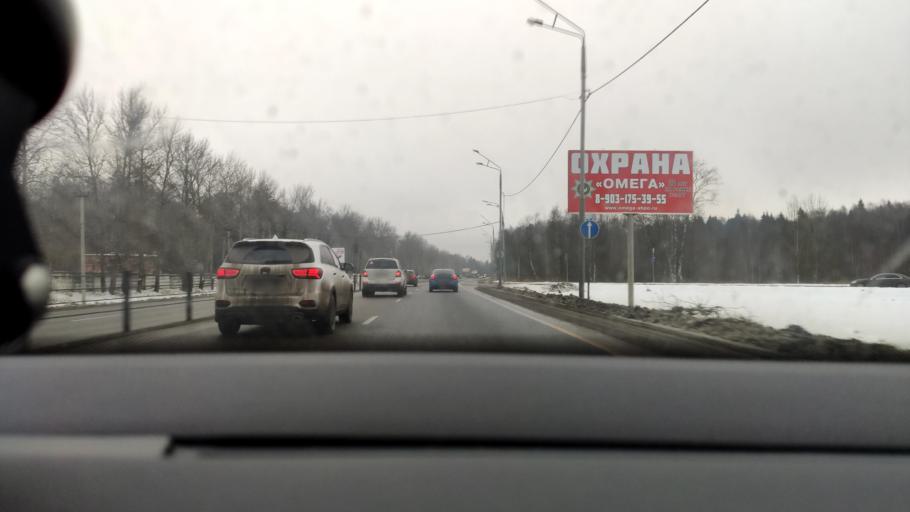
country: RU
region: Moskovskaya
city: Sergiyev Posad
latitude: 56.2523
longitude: 38.1237
